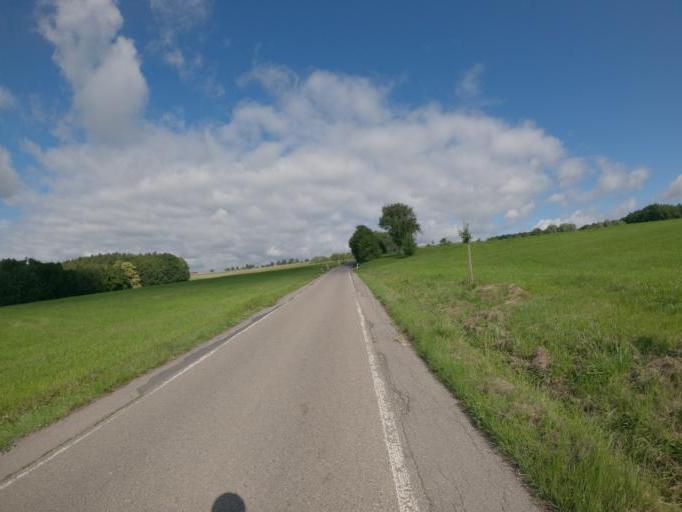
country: DE
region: Baden-Wuerttemberg
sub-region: Regierungsbezirk Stuttgart
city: Ebersbach an der Fils
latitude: 48.7282
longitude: 9.5415
